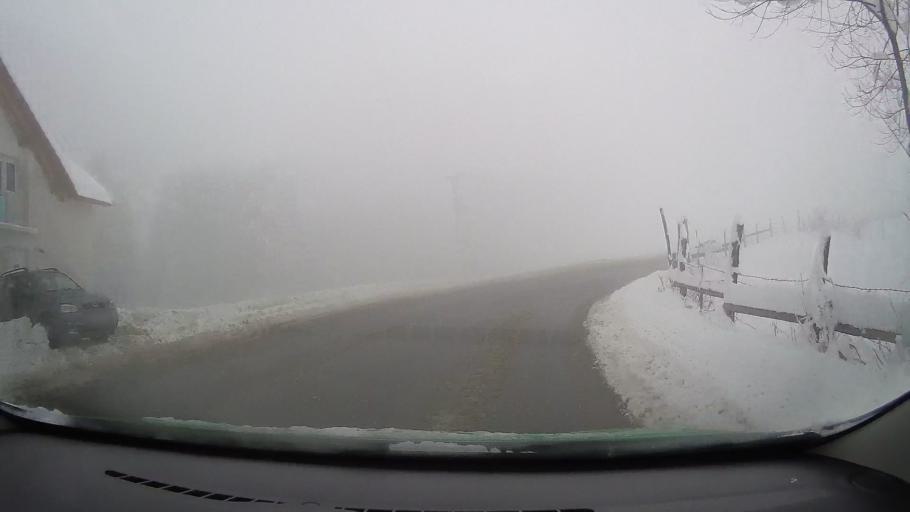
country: RO
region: Sibiu
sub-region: Comuna Jina
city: Jina
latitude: 45.7948
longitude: 23.7018
